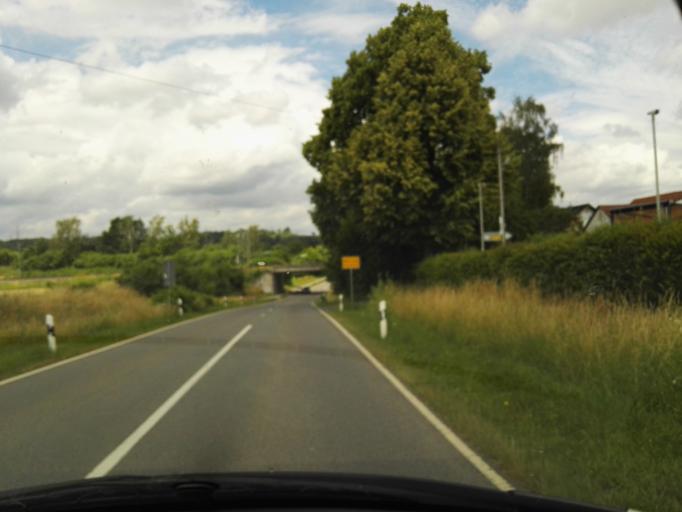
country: DE
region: Bavaria
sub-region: Upper Franconia
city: Redwitz an der Rodach
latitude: 50.1669
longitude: 11.2039
